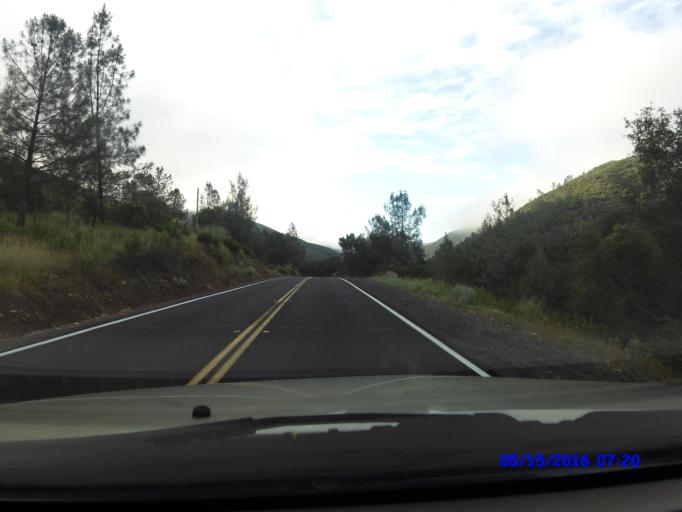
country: US
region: California
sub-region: Tuolumne County
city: Tuolumne City
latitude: 37.7941
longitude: -120.2819
